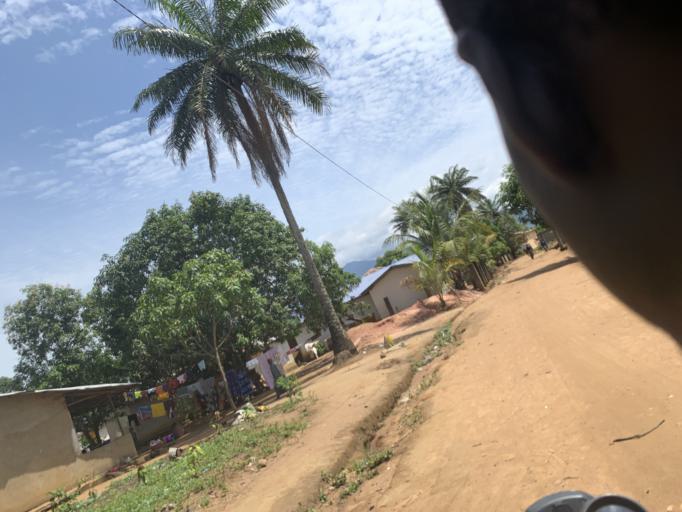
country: SL
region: Western Area
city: Waterloo
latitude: 8.3391
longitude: -13.0514
